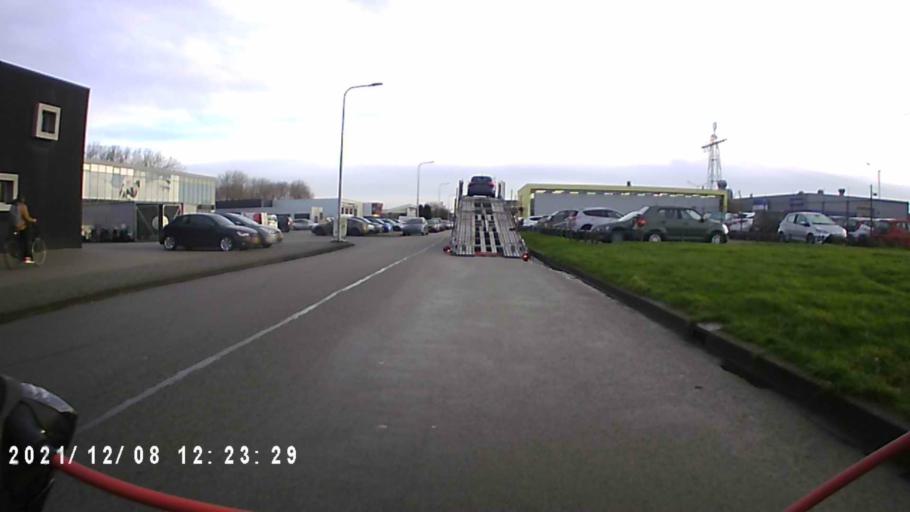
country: NL
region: Groningen
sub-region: Gemeente Groningen
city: Oosterpark
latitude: 53.2216
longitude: 6.6077
